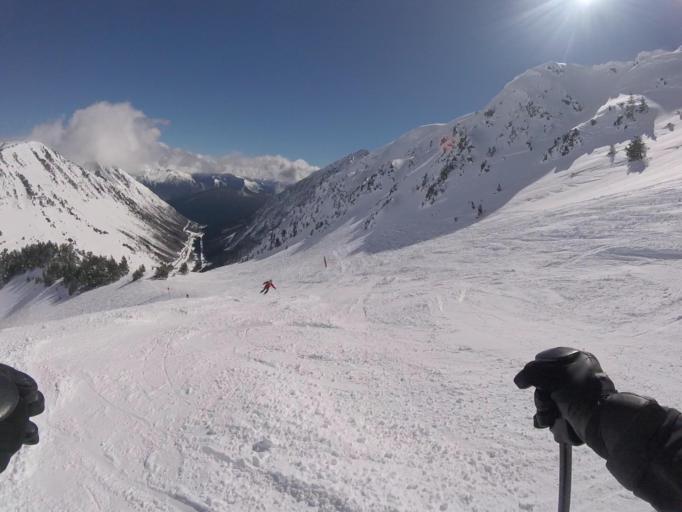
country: ES
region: Catalonia
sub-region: Provincia de Lleida
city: Espot
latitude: 42.6490
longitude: 0.9891
